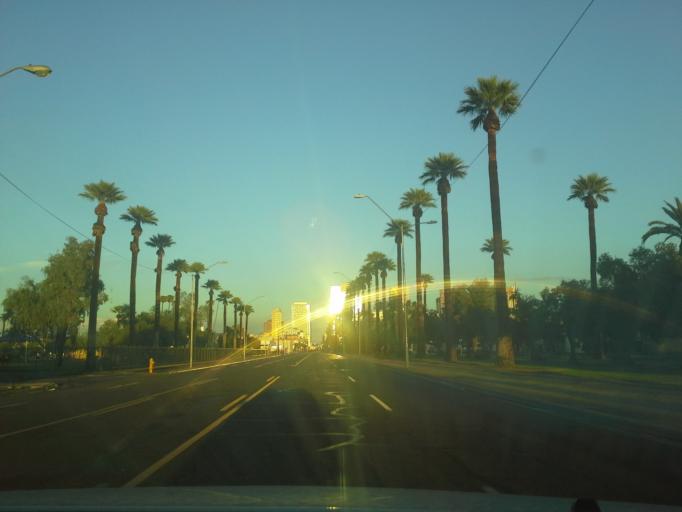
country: US
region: Arizona
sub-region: Maricopa County
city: Phoenix
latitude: 33.4513
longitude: -112.0891
